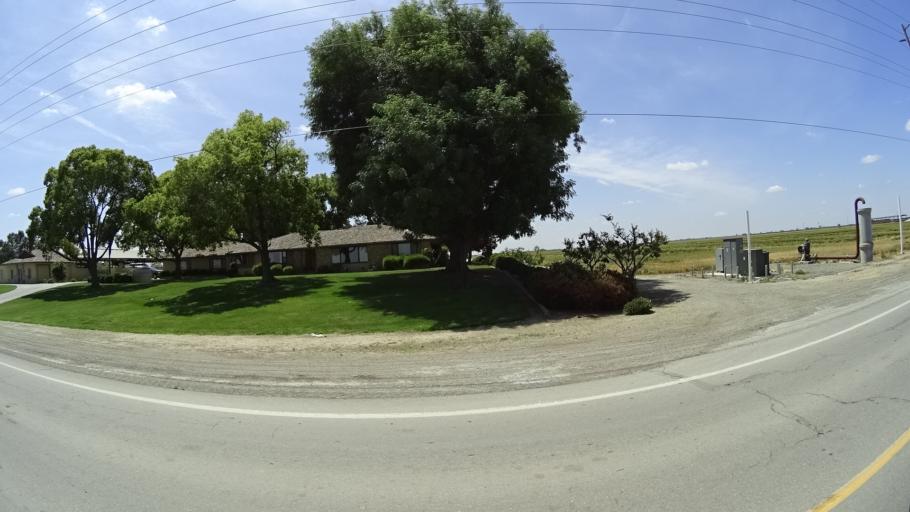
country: US
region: California
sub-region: Kings County
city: Home Garden
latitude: 36.2990
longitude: -119.5329
